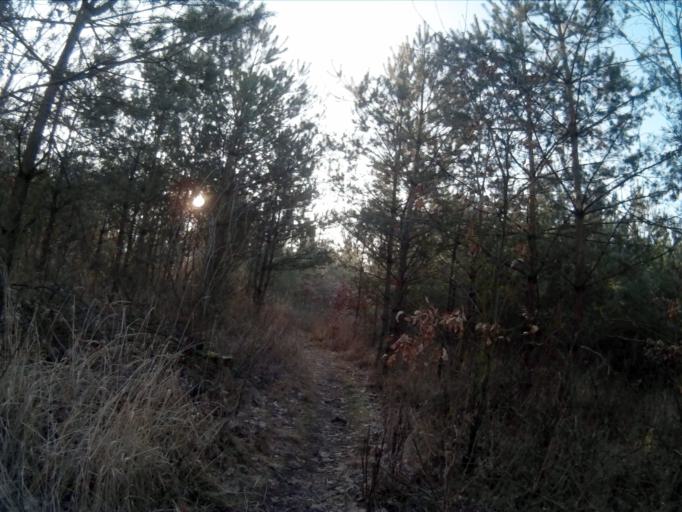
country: CZ
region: Vysocina
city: Namest' nad Oslavou
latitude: 49.1916
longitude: 16.1664
